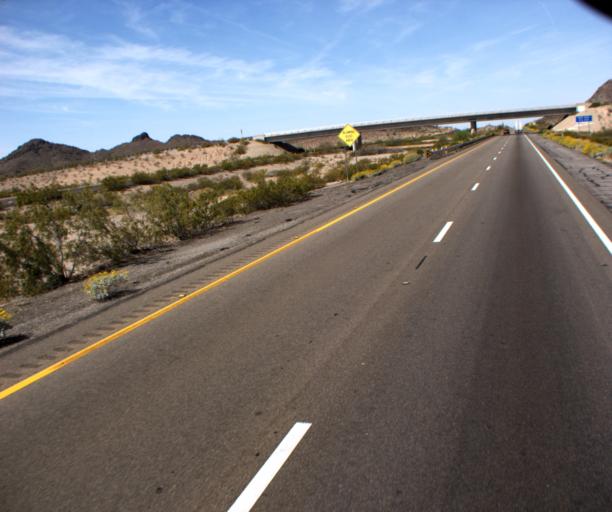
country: US
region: Arizona
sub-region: La Paz County
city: Salome
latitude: 33.6091
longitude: -113.6182
